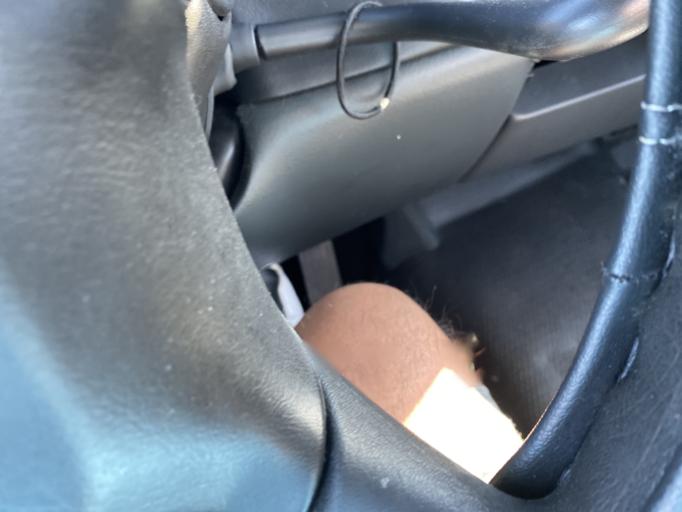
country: US
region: Texas
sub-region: Travis County
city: Garfield
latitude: 30.1677
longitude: -97.6598
